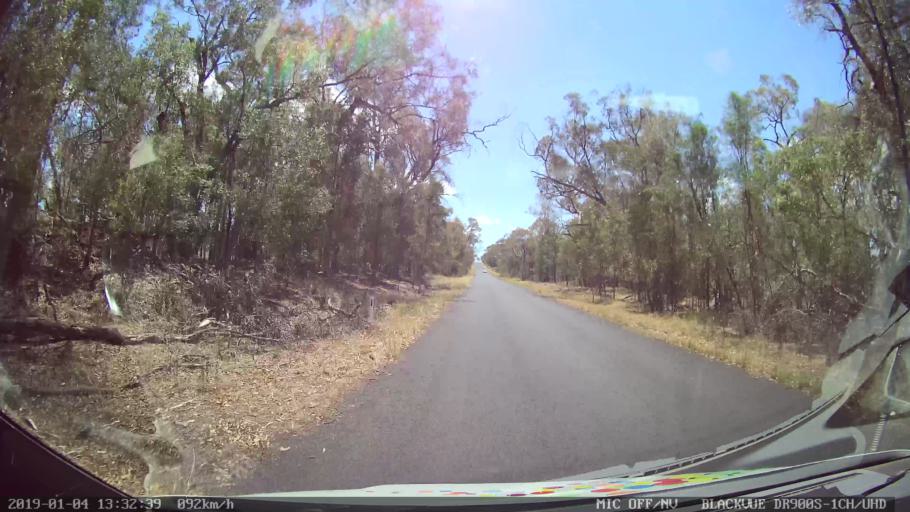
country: AU
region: New South Wales
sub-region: Dubbo Municipality
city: Eulomogo
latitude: -32.6069
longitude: 148.5473
